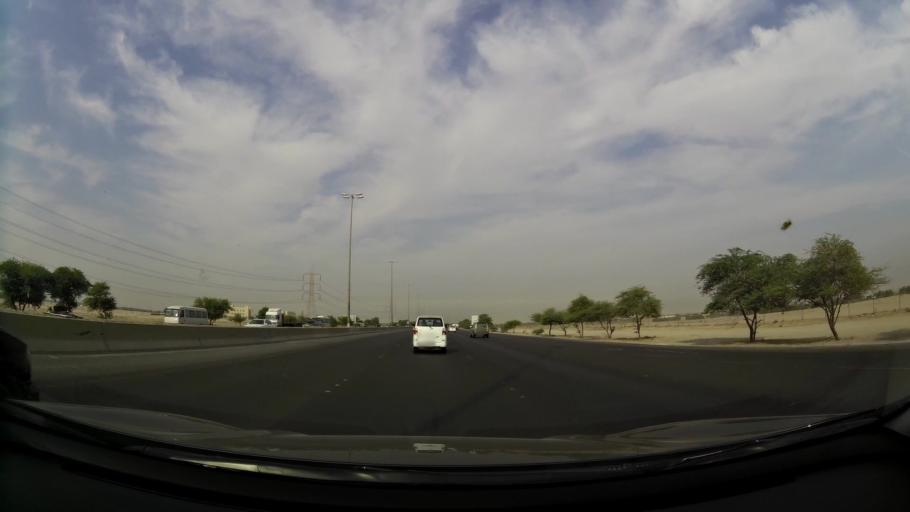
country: KW
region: Al Asimah
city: Ar Rabiyah
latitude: 29.2672
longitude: 47.8302
